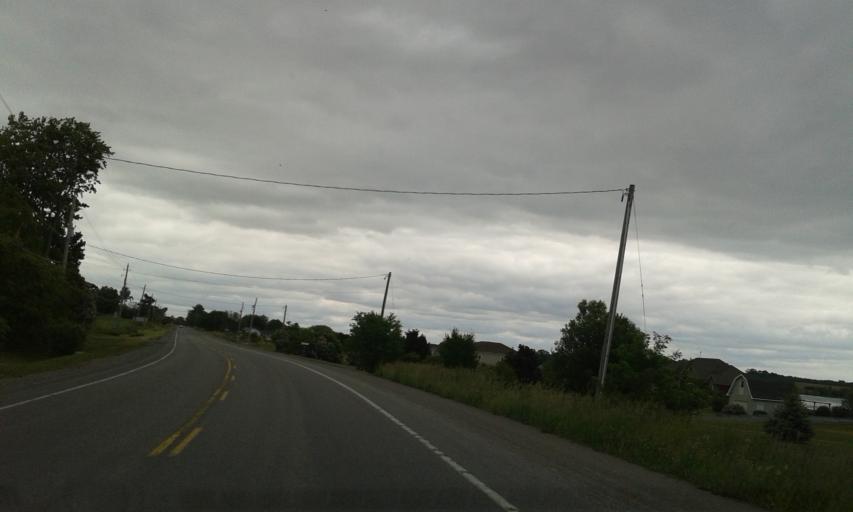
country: CA
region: Ontario
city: Quinte West
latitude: 43.9617
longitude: -77.4955
